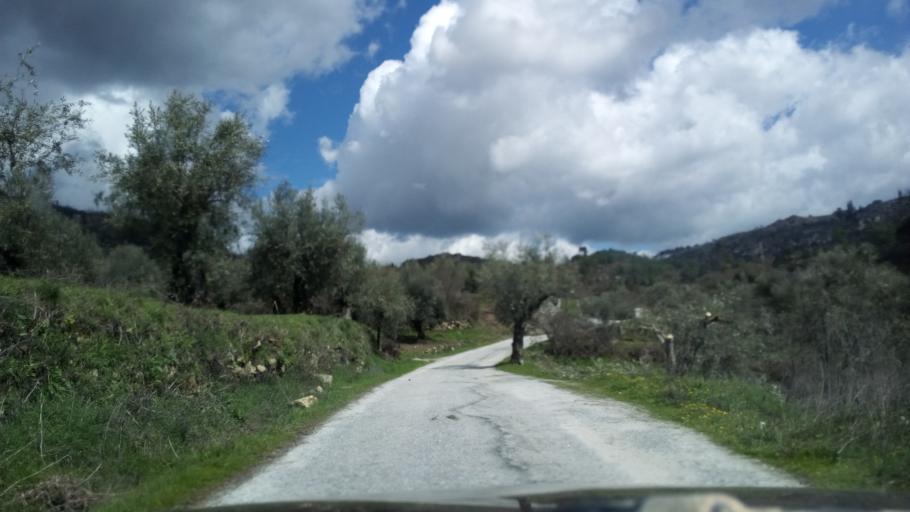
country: PT
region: Guarda
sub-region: Fornos de Algodres
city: Fornos de Algodres
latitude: 40.6606
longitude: -7.4939
